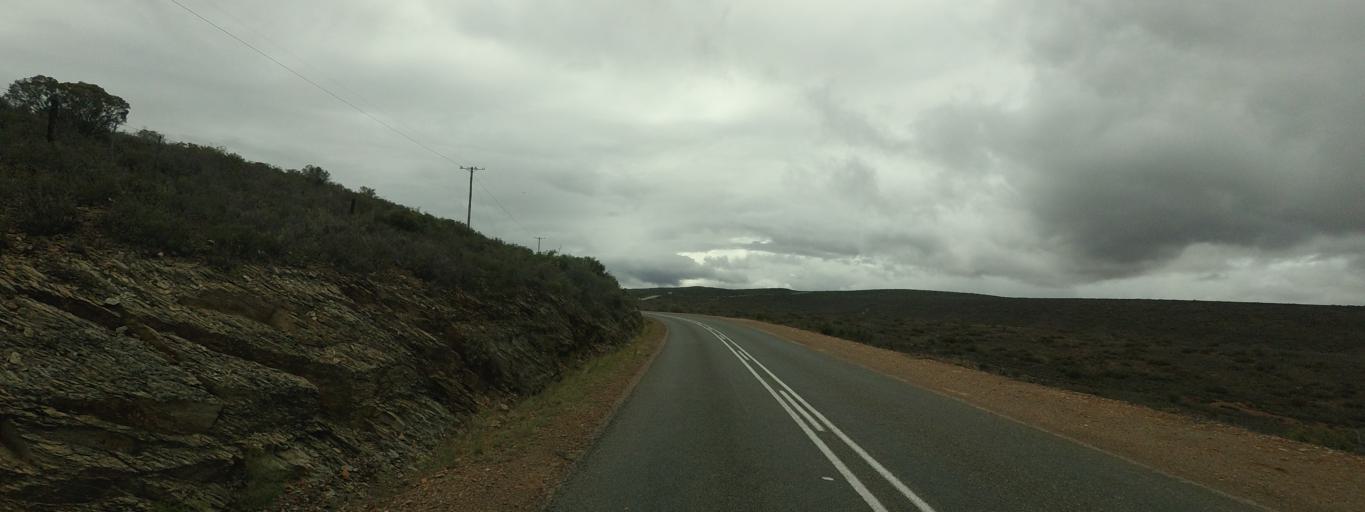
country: ZA
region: Western Cape
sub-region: Eden District Municipality
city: Oudtshoorn
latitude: -33.6912
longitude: 22.2693
